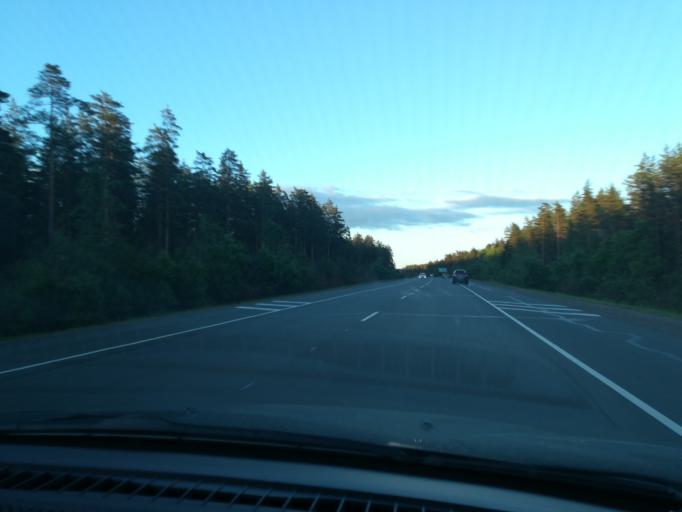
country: RU
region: Leningrad
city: Yakovlevo
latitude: 60.3607
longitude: 29.5766
